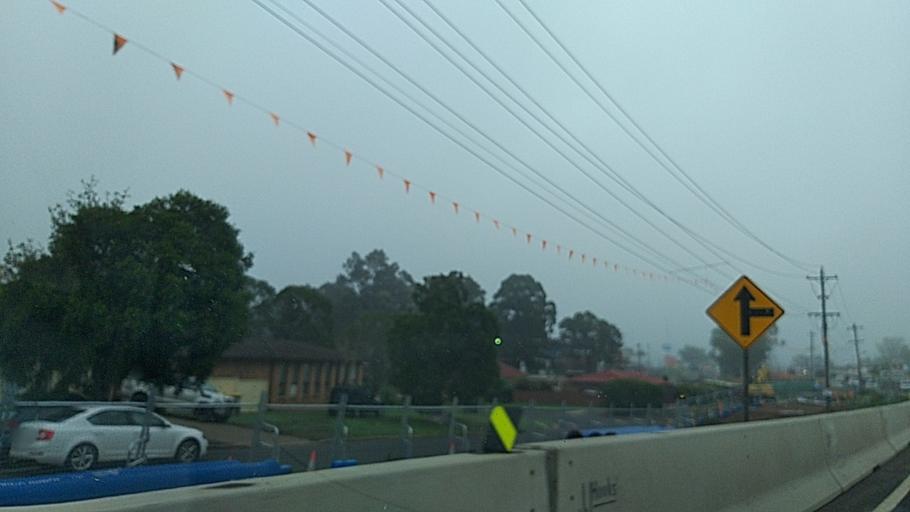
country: AU
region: New South Wales
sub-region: Penrith Municipality
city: Kingswood Park
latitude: -33.7797
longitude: 150.7108
